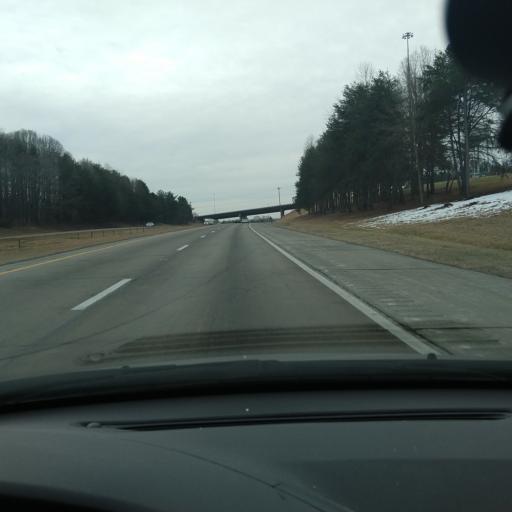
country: US
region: North Carolina
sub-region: Davidson County
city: Midway
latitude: 35.9732
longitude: -80.2307
